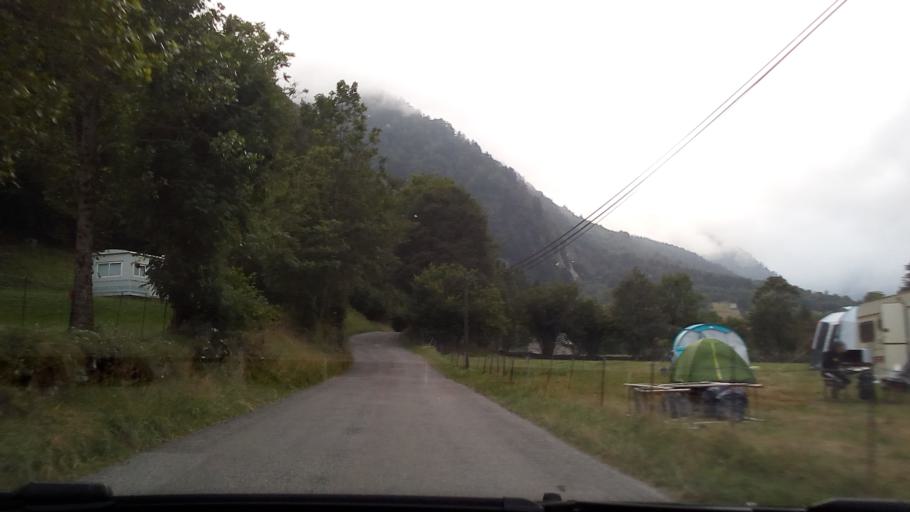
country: FR
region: Midi-Pyrenees
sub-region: Departement des Hautes-Pyrenees
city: Cauterets
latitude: 42.9164
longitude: -0.1893
